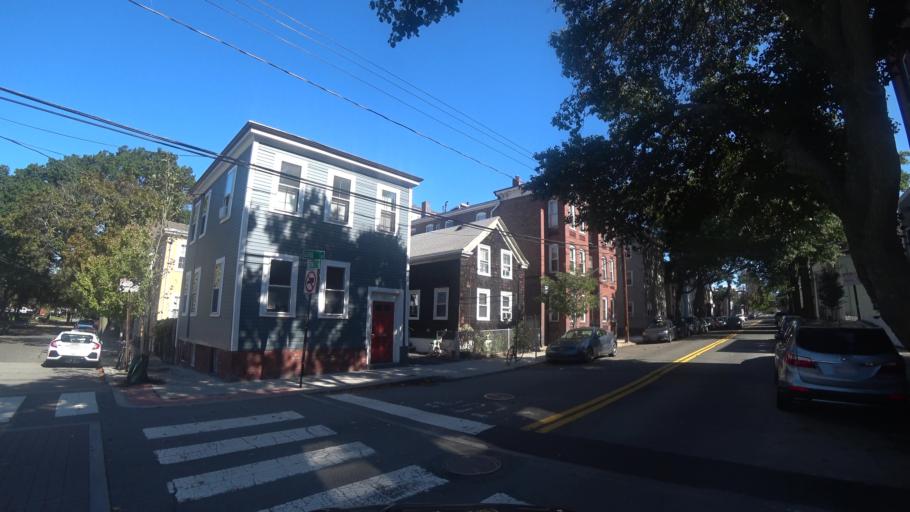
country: US
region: Massachusetts
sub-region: Middlesex County
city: Somerville
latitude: 42.3721
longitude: -71.0829
